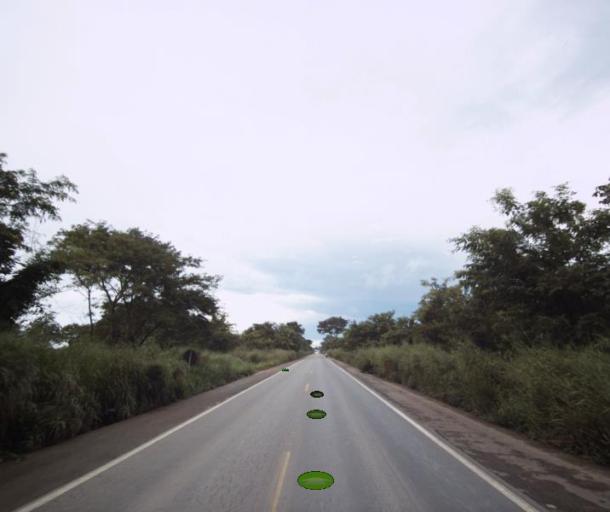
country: BR
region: Goias
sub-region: Porangatu
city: Porangatu
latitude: -13.5545
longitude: -49.0769
